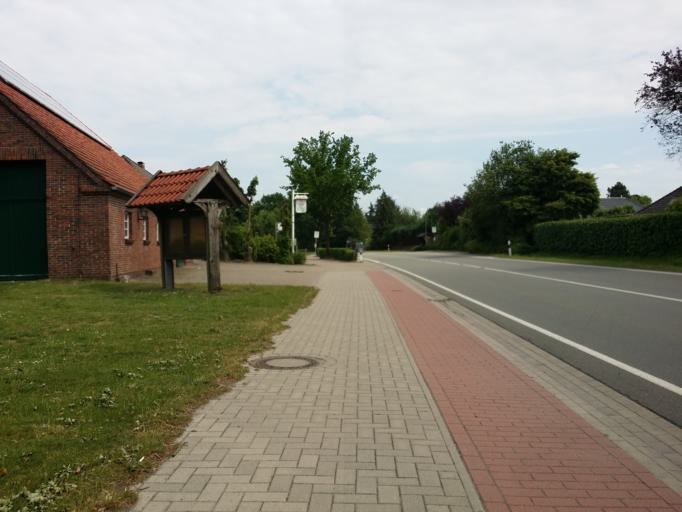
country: DE
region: Lower Saxony
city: Wiefelstede
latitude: 53.2453
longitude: 8.1414
